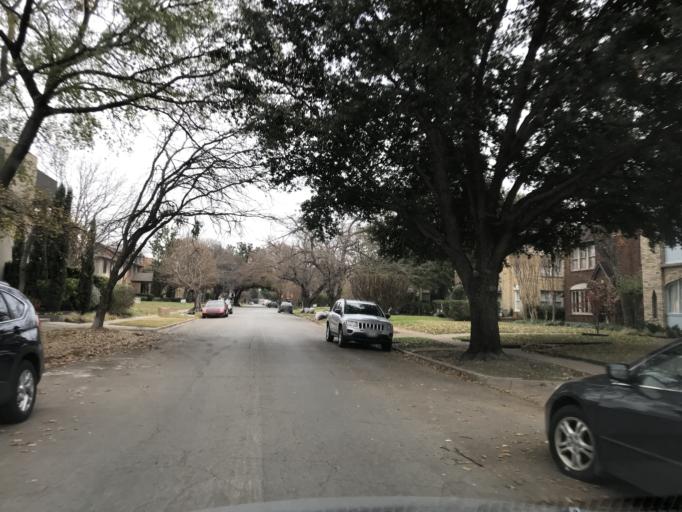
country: US
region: Texas
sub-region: Dallas County
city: Highland Park
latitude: 32.8217
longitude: -96.8083
